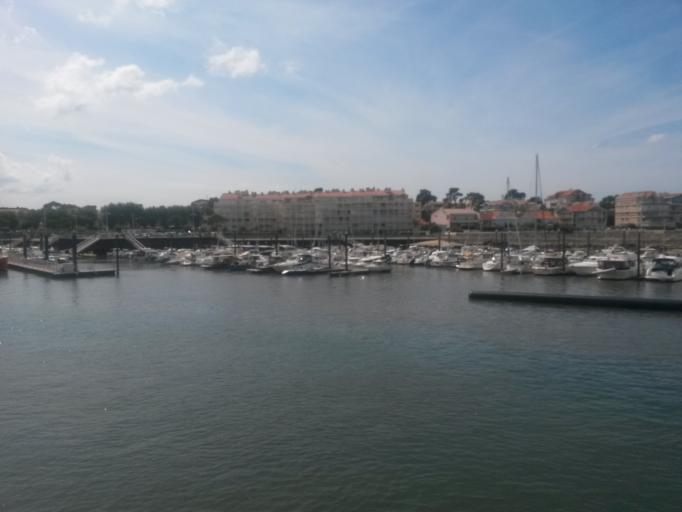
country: FR
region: Aquitaine
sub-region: Departement de la Gironde
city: Arcachon
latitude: 44.6621
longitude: -1.1514
